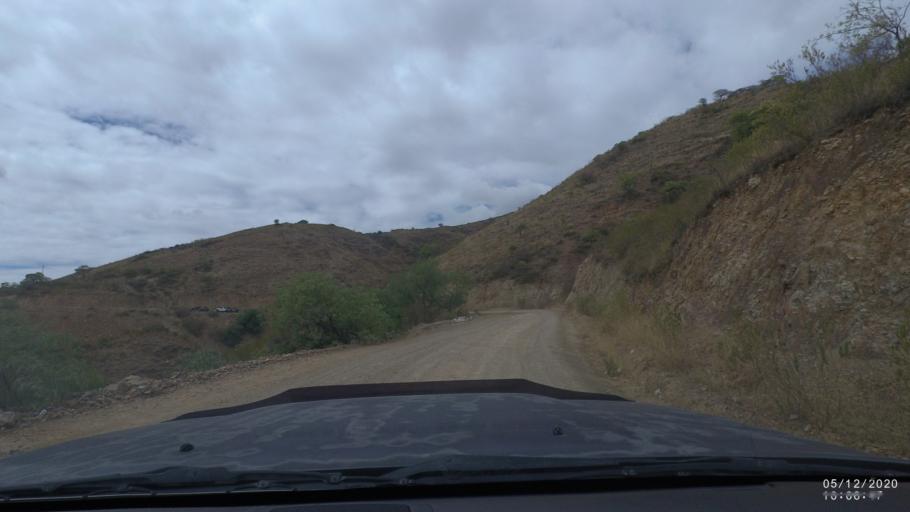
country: BO
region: Cochabamba
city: Sipe Sipe
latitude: -17.4779
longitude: -66.2840
